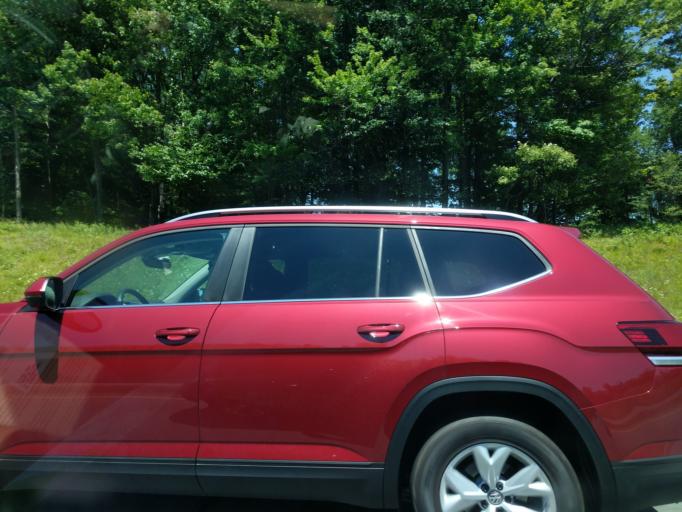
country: US
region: New York
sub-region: Sullivan County
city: Monticello
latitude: 41.6566
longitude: -74.6684
